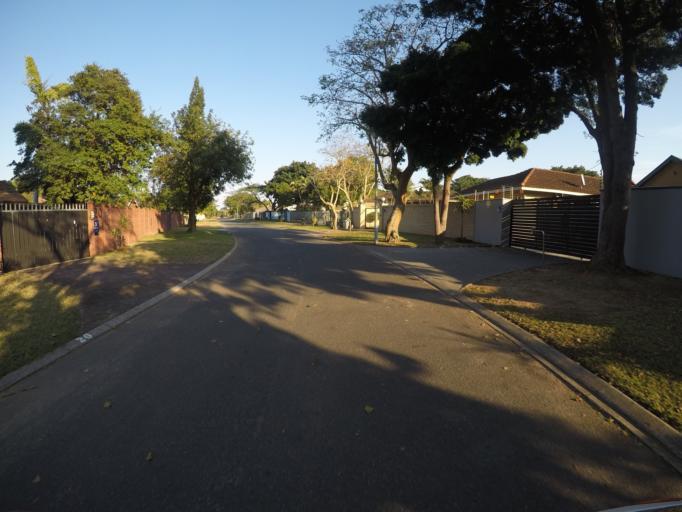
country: ZA
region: KwaZulu-Natal
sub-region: uThungulu District Municipality
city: Richards Bay
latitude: -28.7790
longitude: 32.1140
